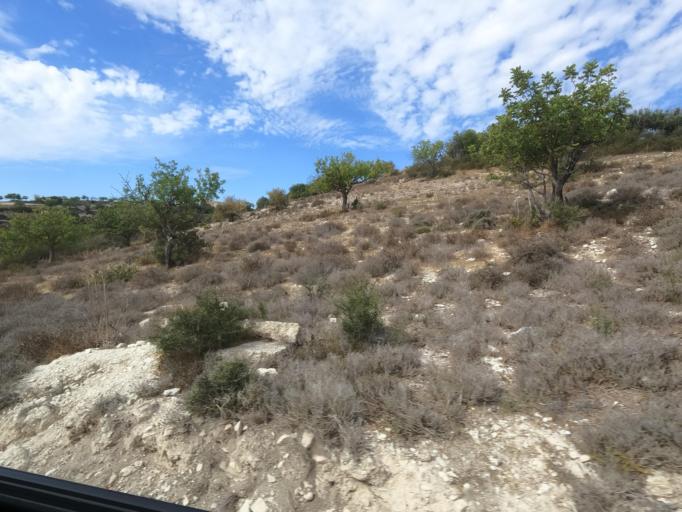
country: CY
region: Pafos
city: Mesogi
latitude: 34.8150
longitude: 32.4673
